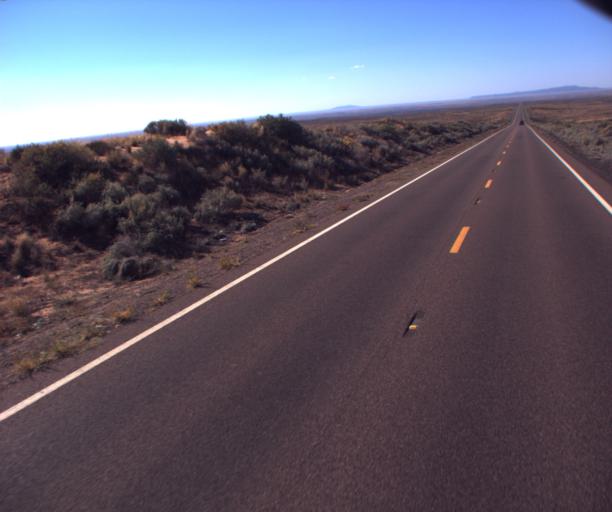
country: US
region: Arizona
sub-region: Navajo County
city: Winslow
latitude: 35.0619
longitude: -110.5829
